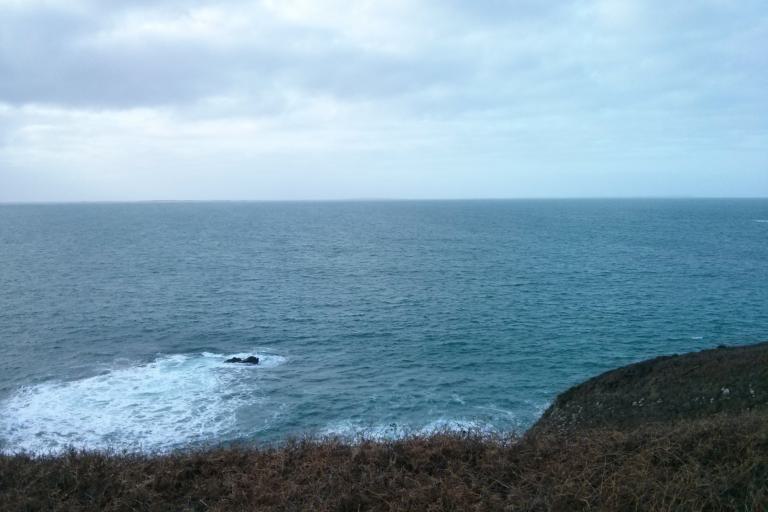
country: FR
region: Brittany
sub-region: Departement du Finistere
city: Le Conquet
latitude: 48.4008
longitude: -4.7742
